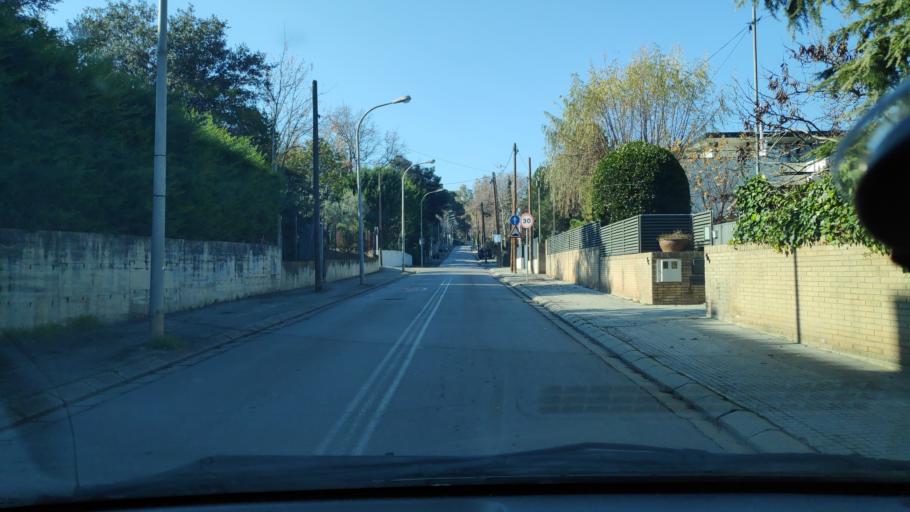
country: ES
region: Catalonia
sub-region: Provincia de Barcelona
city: Sant Quirze del Valles
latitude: 41.5064
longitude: 2.0861
